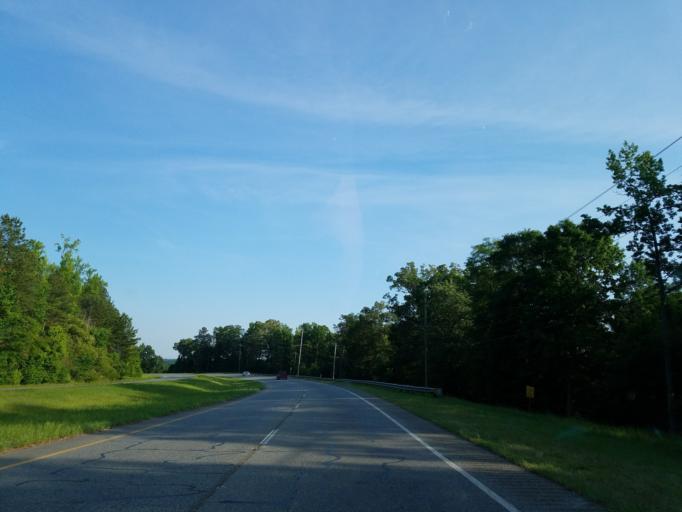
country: US
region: Georgia
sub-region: Chattooga County
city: Summerville
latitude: 34.4045
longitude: -85.2161
